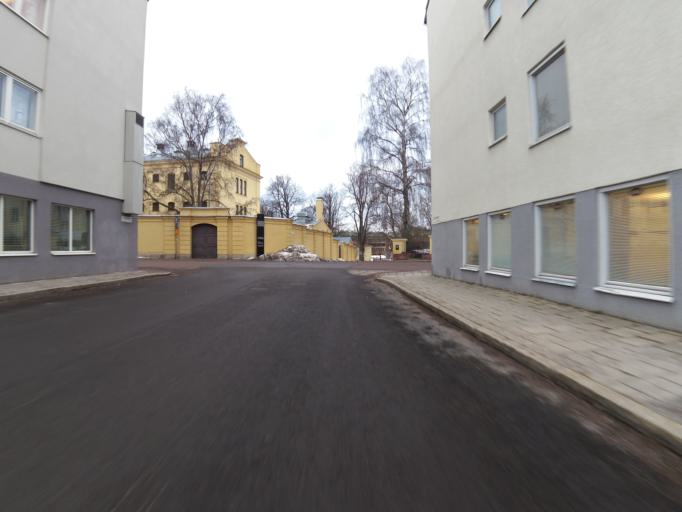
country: SE
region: Gaevleborg
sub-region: Gavle Kommun
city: Gavle
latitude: 60.6712
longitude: 17.1439
